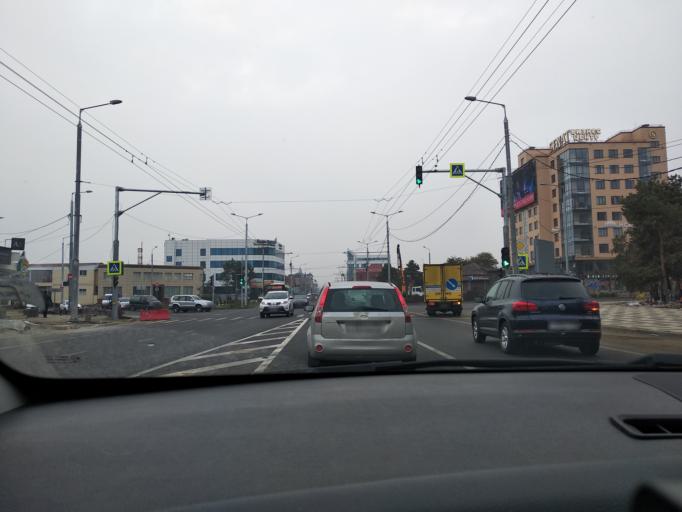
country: RU
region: Krasnodarskiy
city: Krasnodar
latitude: 45.0516
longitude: 38.9592
